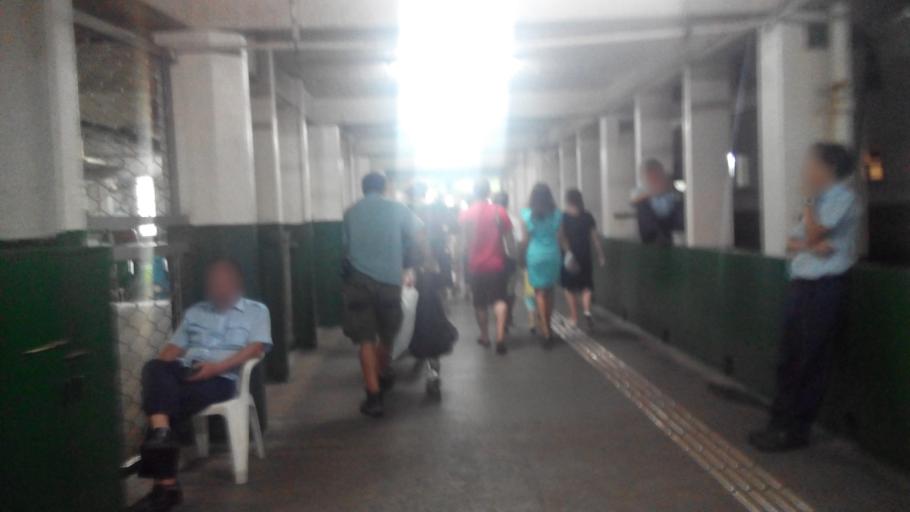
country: HK
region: Wanchai
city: Wan Chai
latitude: 22.2938
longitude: 114.1682
